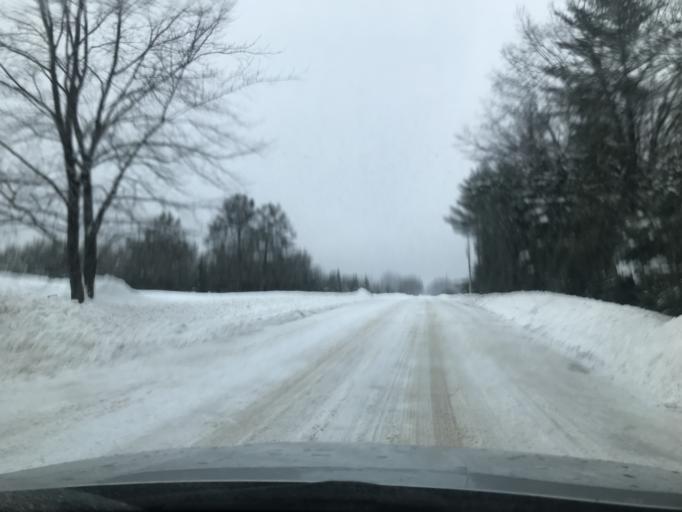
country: US
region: Wisconsin
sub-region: Marinette County
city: Peshtigo
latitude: 45.3812
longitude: -87.9328
